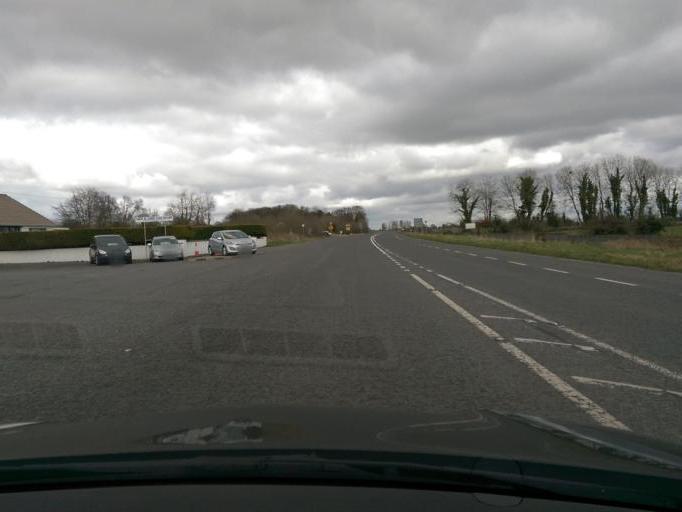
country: IE
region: Leinster
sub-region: An Iarmhi
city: Athlone
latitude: 53.3618
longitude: -8.0675
